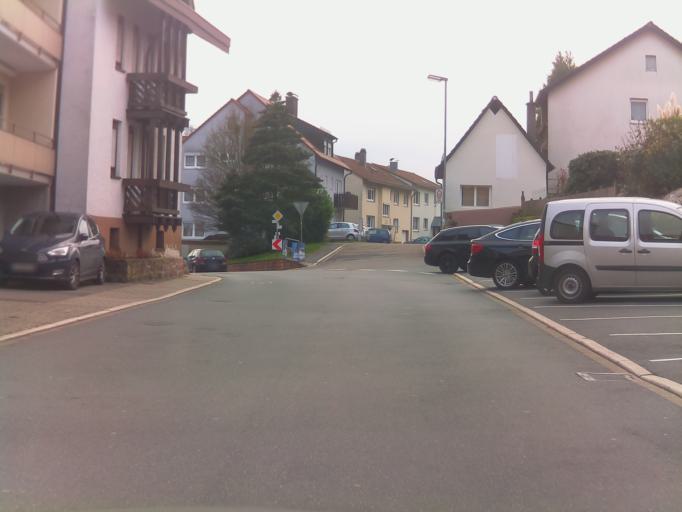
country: DE
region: Baden-Wuerttemberg
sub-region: Karlsruhe Region
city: Bammental
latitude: 49.3731
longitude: 8.7703
